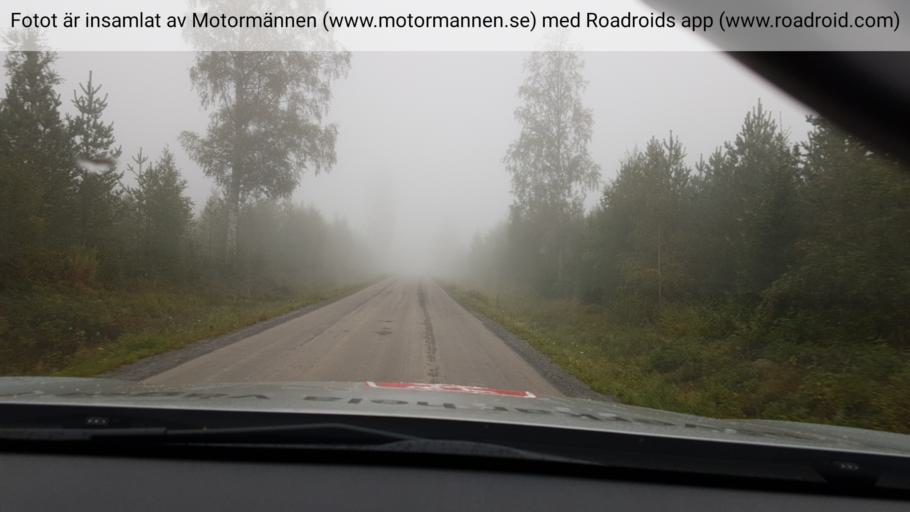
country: SE
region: Vaesterbotten
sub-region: Umea Kommun
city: Ersmark
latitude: 64.0967
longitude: 20.2478
